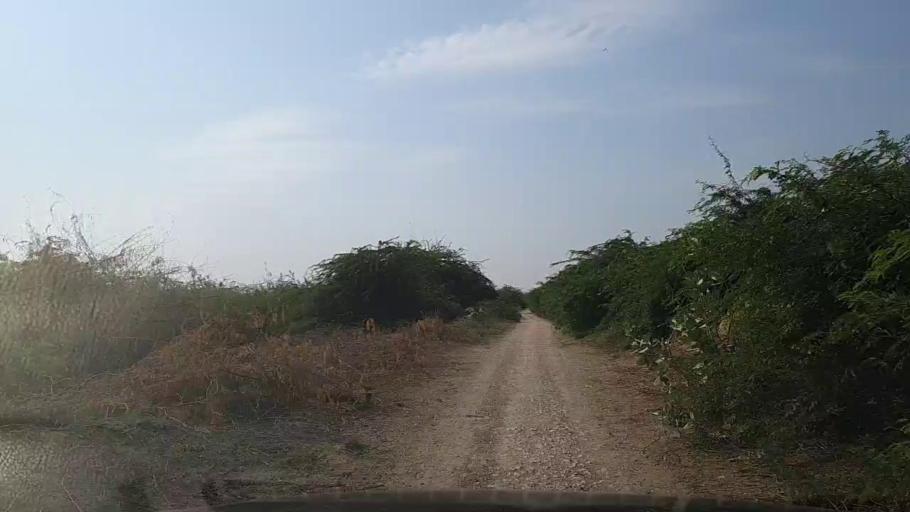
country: PK
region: Sindh
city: Thatta
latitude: 24.7711
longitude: 67.8147
